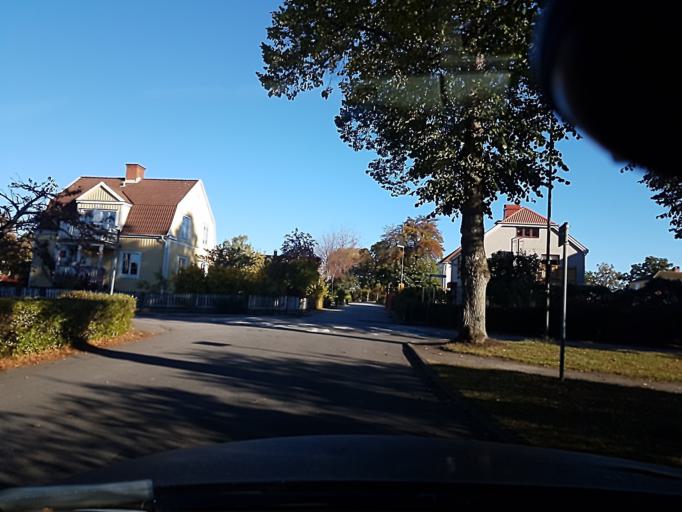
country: SE
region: Kronoberg
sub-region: Vaxjo Kommun
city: Vaexjoe
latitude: 56.8762
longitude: 14.8224
